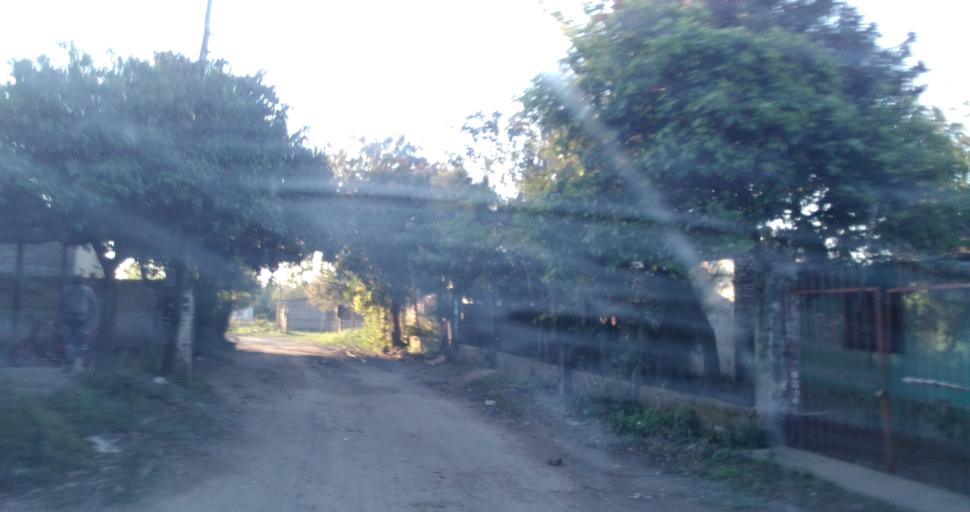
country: AR
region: Chaco
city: Fontana
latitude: -27.4206
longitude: -59.0169
